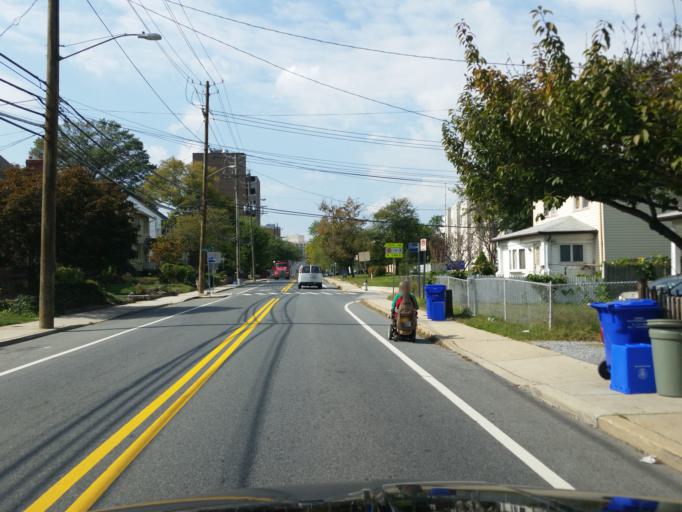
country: US
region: Maryland
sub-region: Montgomery County
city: Silver Spring
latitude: 38.9902
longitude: -77.0213
